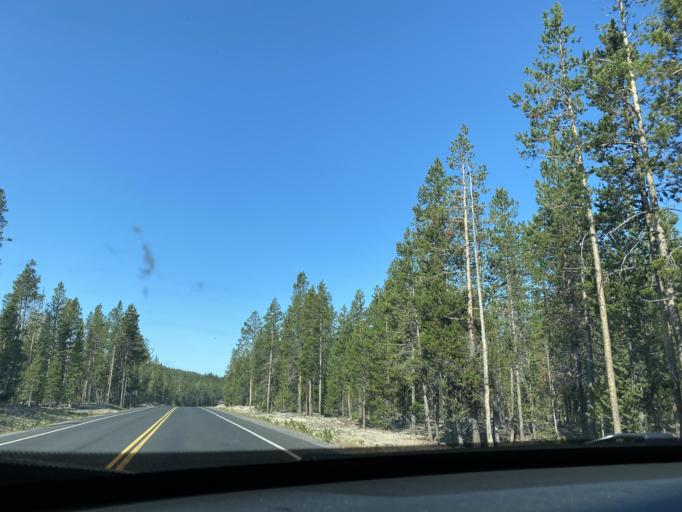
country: US
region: Oregon
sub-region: Deschutes County
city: Three Rivers
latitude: 43.7057
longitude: -121.2451
